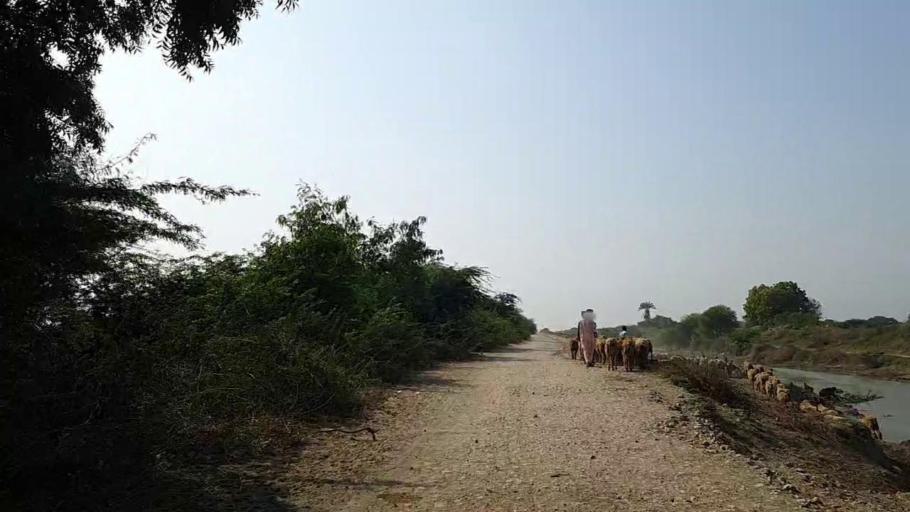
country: PK
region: Sindh
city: Mirpur Sakro
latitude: 24.6378
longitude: 67.7392
